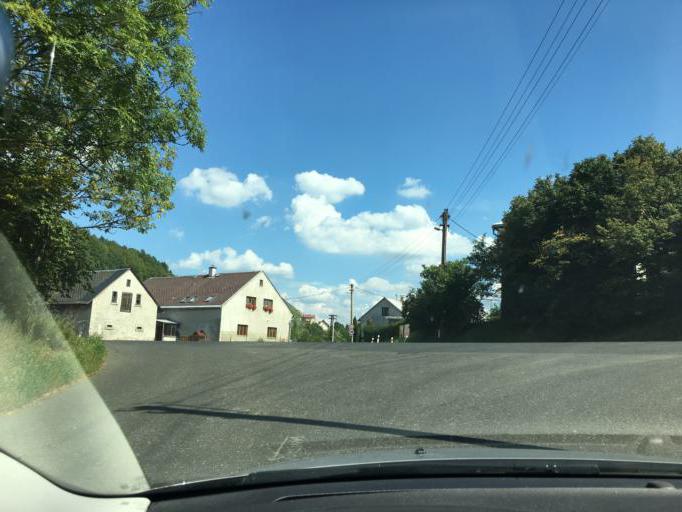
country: CZ
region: Liberecky
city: Mala Skala
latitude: 50.6520
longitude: 15.1556
